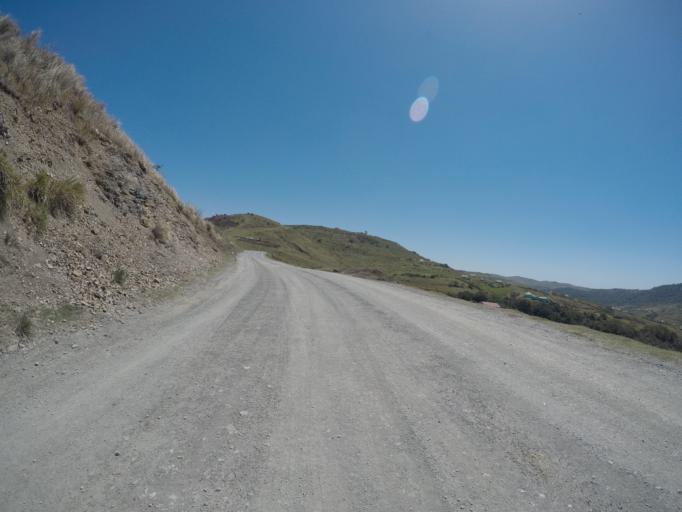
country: ZA
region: Eastern Cape
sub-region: OR Tambo District Municipality
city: Libode
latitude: -32.0139
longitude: 29.0771
